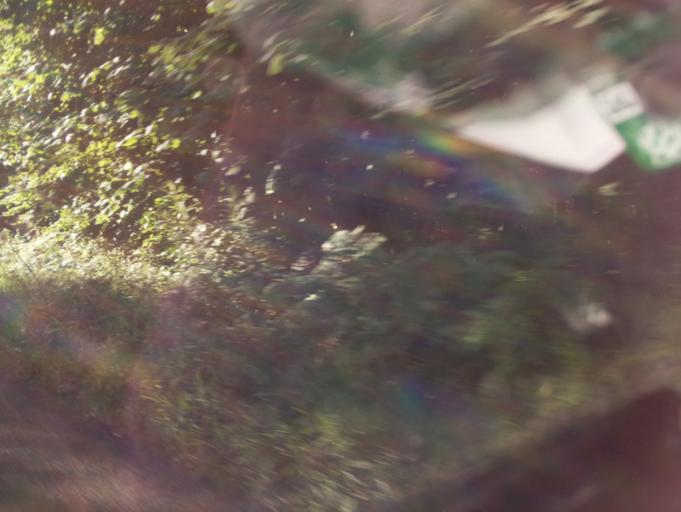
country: GB
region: Wales
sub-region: Monmouthshire
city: Chepstow
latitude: 51.6496
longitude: -2.6994
